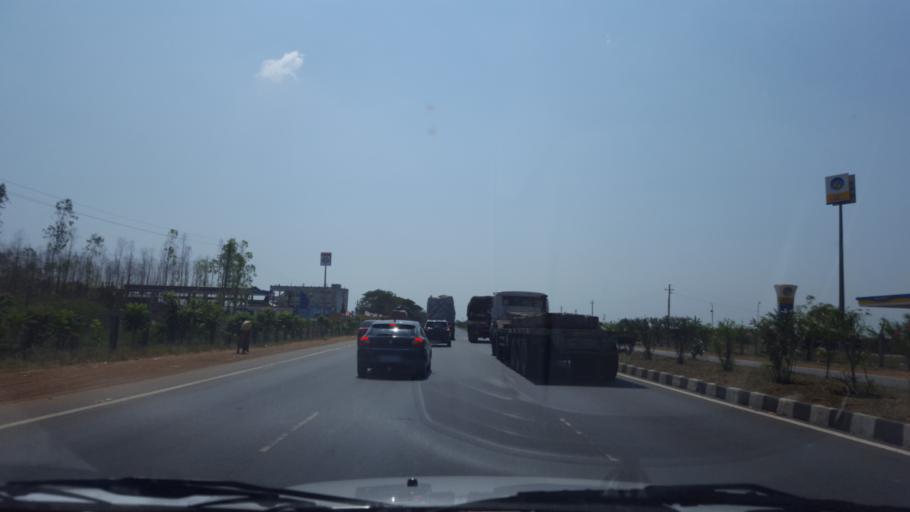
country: IN
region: Andhra Pradesh
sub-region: Prakasam
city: Ongole
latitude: 15.4086
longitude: 80.0394
